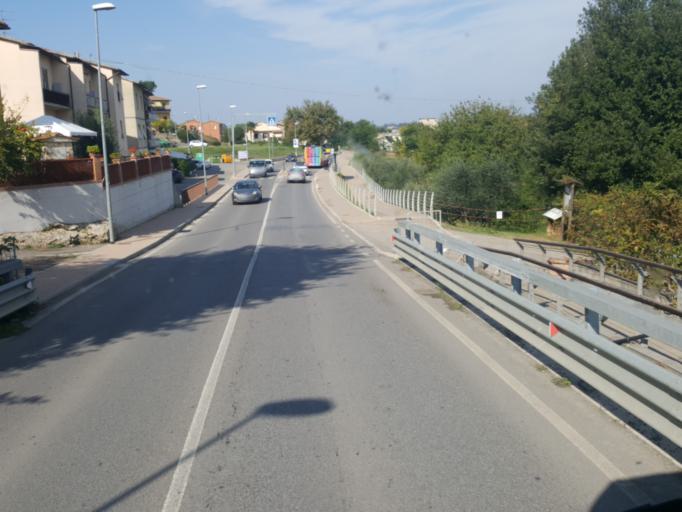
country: IT
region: Tuscany
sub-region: Provincia di Siena
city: Colle di Val d'Elsa
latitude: 43.4038
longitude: 11.1343
